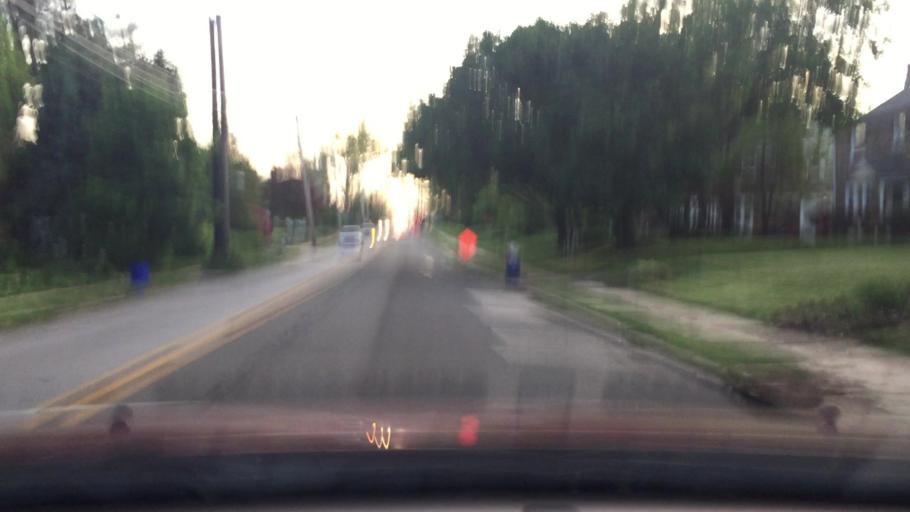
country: US
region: Pennsylvania
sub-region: Delaware County
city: Drexel Hill
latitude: 39.9483
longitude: -75.2889
